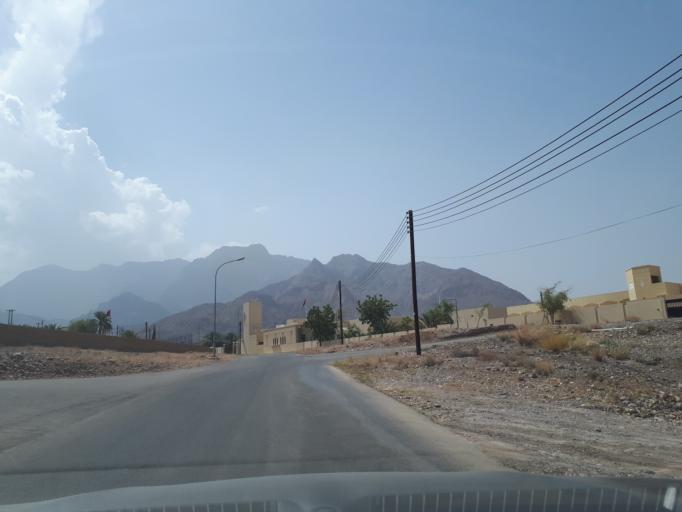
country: OM
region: Ash Sharqiyah
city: Ibra'
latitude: 23.0866
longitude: 58.8655
